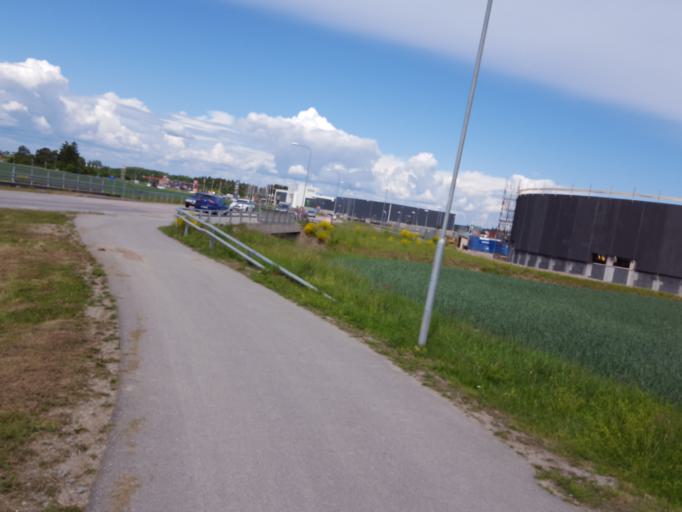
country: SE
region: Uppsala
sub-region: Uppsala Kommun
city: Uppsala
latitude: 59.8820
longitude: 17.6730
